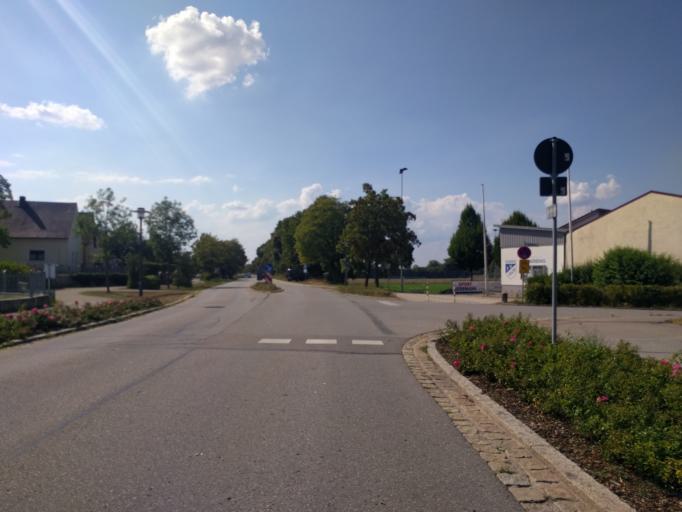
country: DE
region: Bavaria
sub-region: Upper Palatinate
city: Barbing
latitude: 49.0043
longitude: 12.1936
